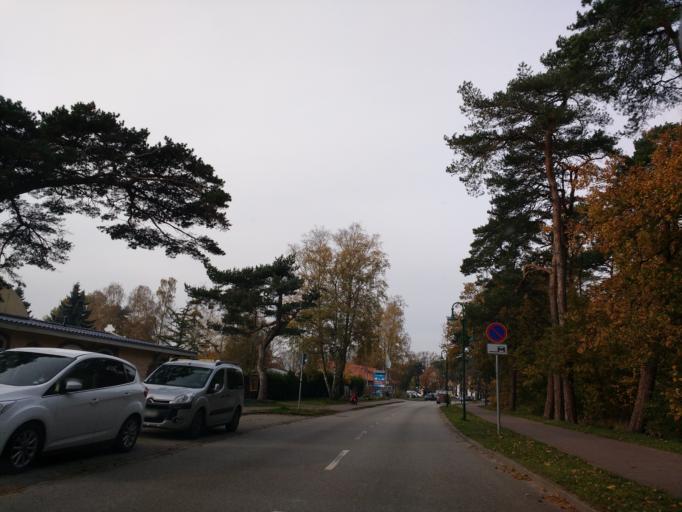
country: DE
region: Mecklenburg-Vorpommern
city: Ostseebad Boltenhagen
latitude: 53.9815
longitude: 11.2188
